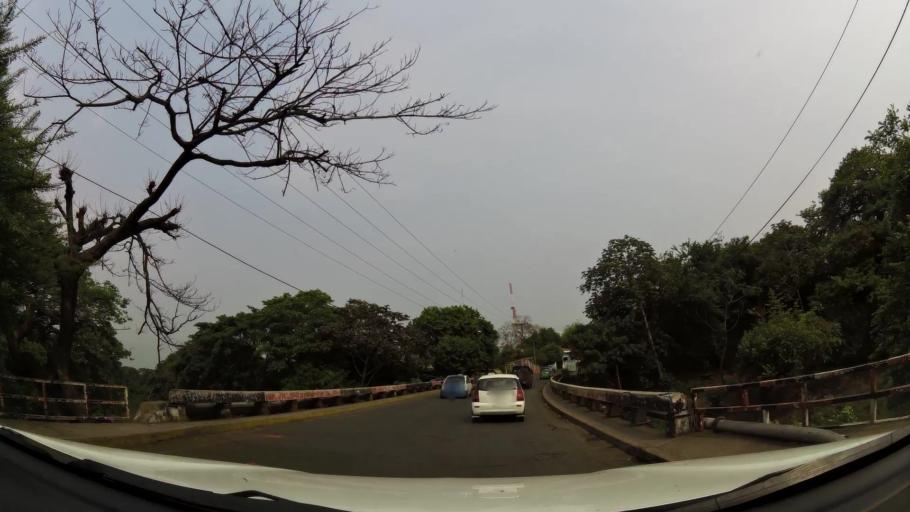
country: NI
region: Chinandega
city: Chinandega
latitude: 12.6350
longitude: -87.1356
